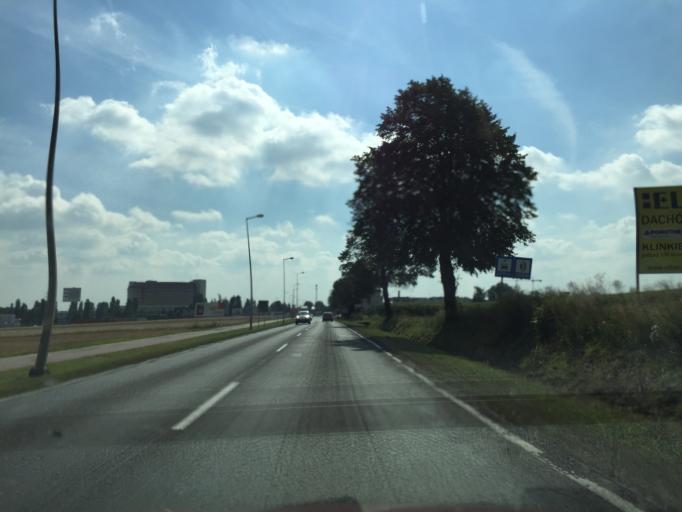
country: PL
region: Greater Poland Voivodeship
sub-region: Kalisz
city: Kalisz
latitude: 51.7659
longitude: 18.0565
